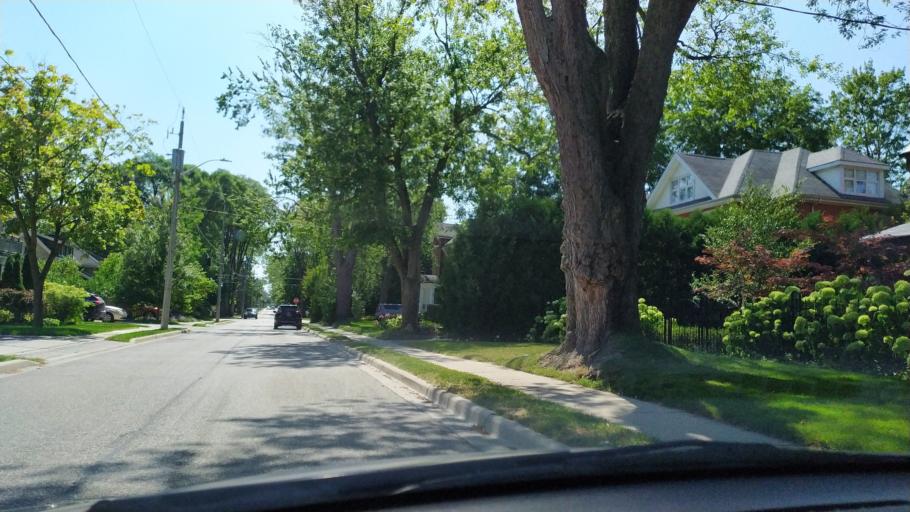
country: CA
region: Ontario
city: Stratford
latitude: 43.3668
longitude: -80.9882
